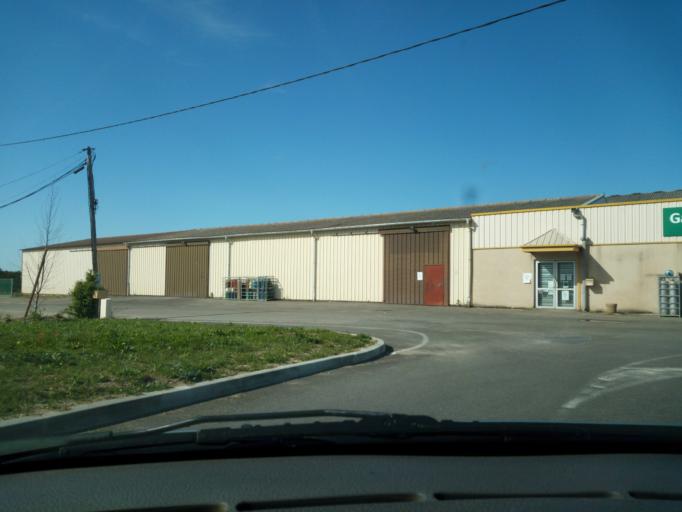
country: FR
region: Midi-Pyrenees
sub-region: Departement du Lot
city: Castelnau-Montratier
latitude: 44.2809
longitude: 1.3587
